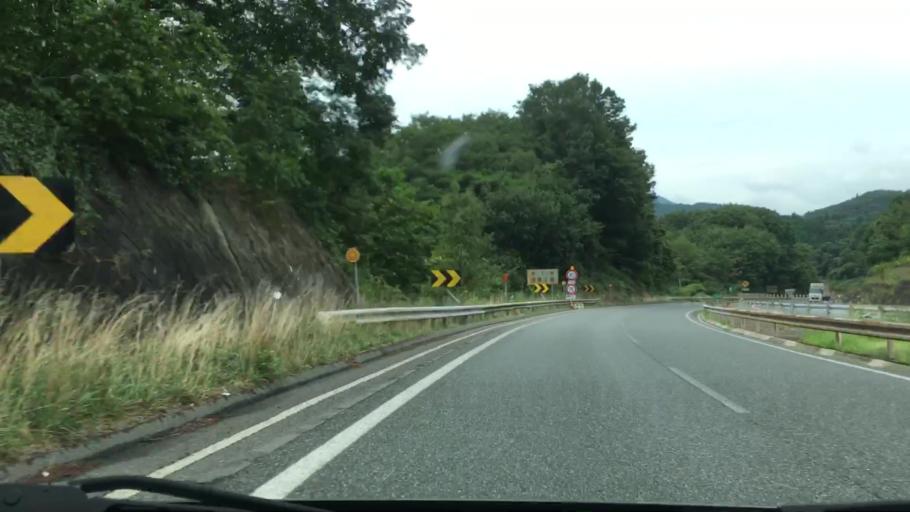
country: JP
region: Okayama
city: Niimi
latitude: 35.0149
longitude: 133.5846
